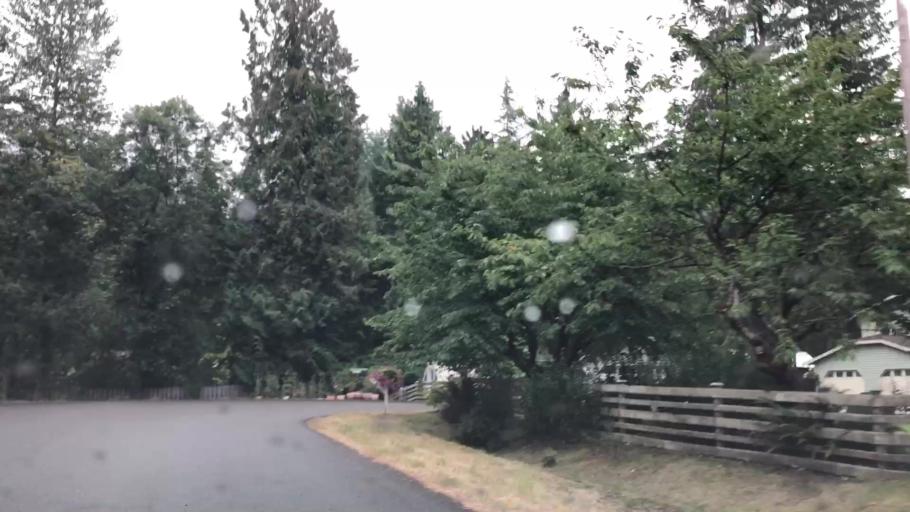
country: US
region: Washington
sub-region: King County
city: Cottage Lake
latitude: 47.7558
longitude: -122.0629
